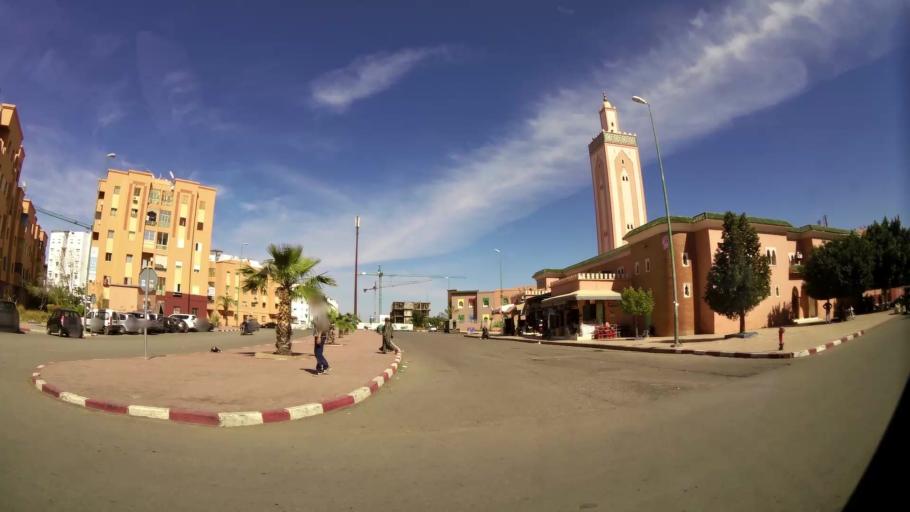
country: MA
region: Marrakech-Tensift-Al Haouz
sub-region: Marrakech
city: Marrakesh
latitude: 31.6760
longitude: -8.0175
